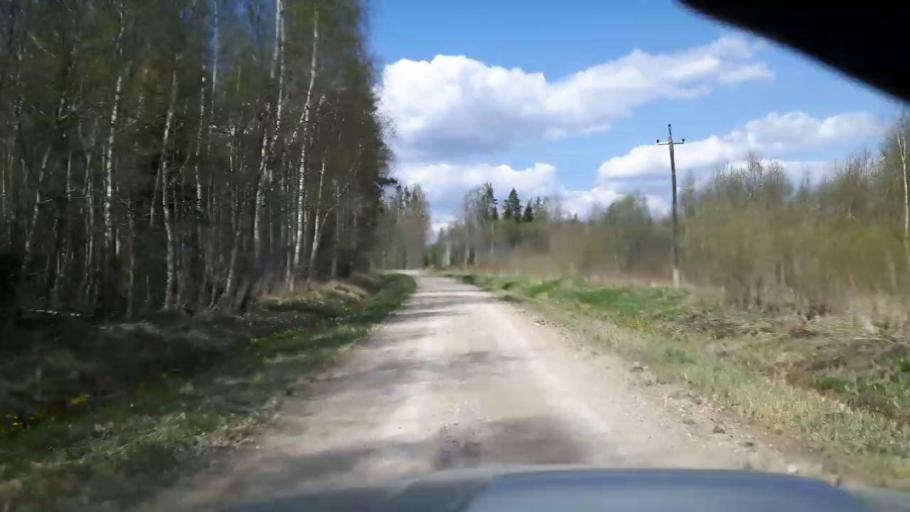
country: EE
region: Paernumaa
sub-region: Tootsi vald
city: Tootsi
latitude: 58.4523
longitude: 24.8946
